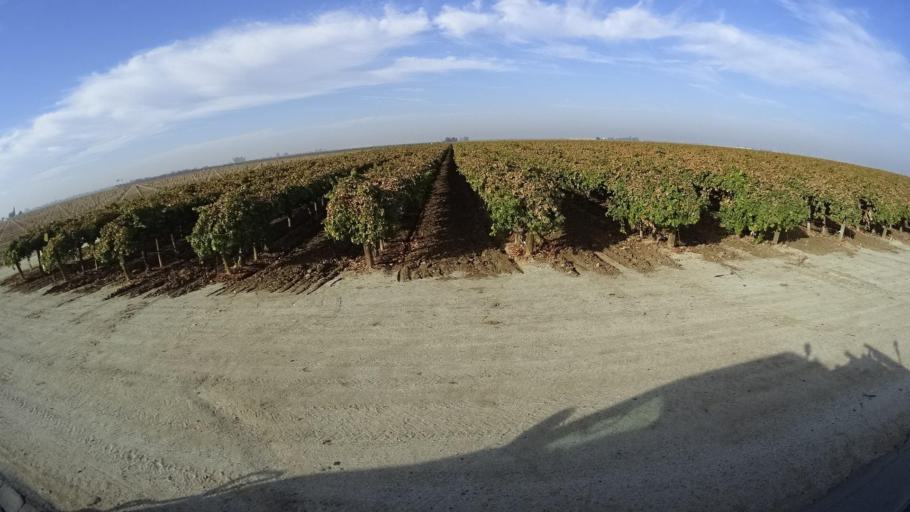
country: US
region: California
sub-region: Kern County
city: McFarland
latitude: 35.6966
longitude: -119.2049
